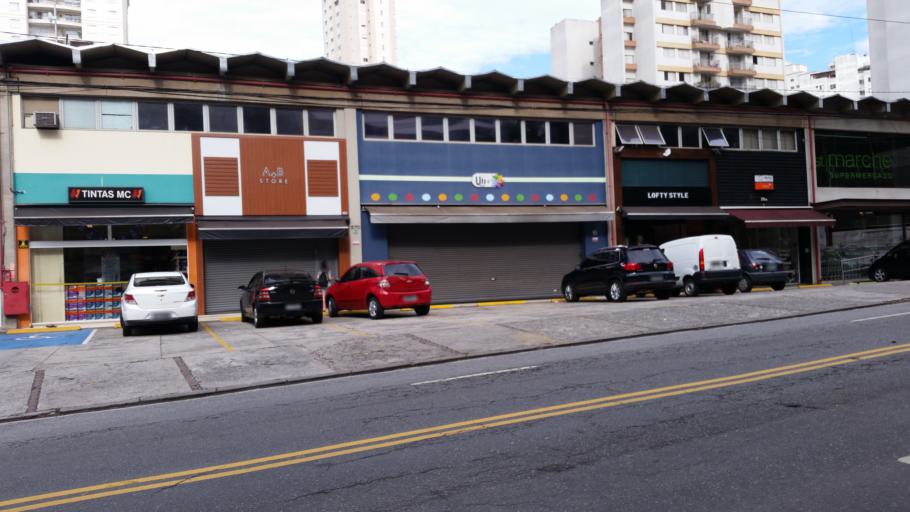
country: BR
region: Sao Paulo
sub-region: Diadema
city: Diadema
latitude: -23.6578
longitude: -46.6915
